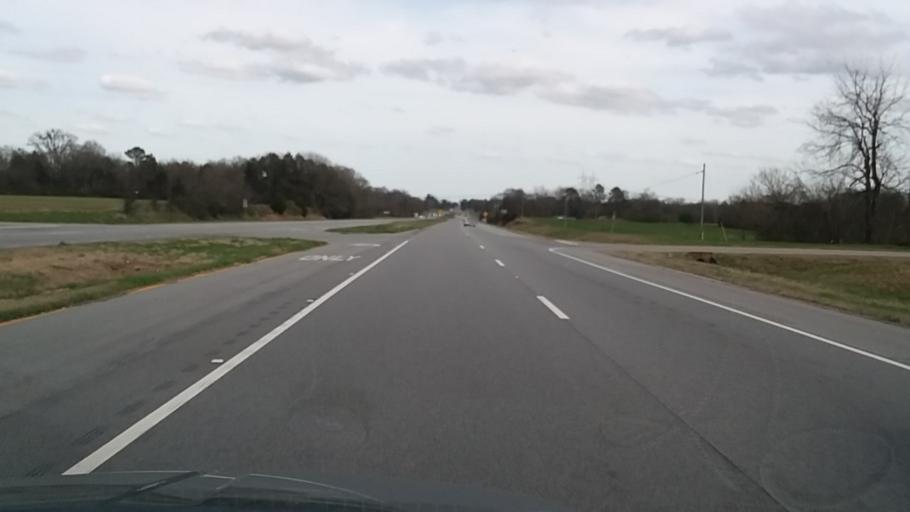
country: US
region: Alabama
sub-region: Lawrence County
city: Town Creek
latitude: 34.6824
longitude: -87.4591
